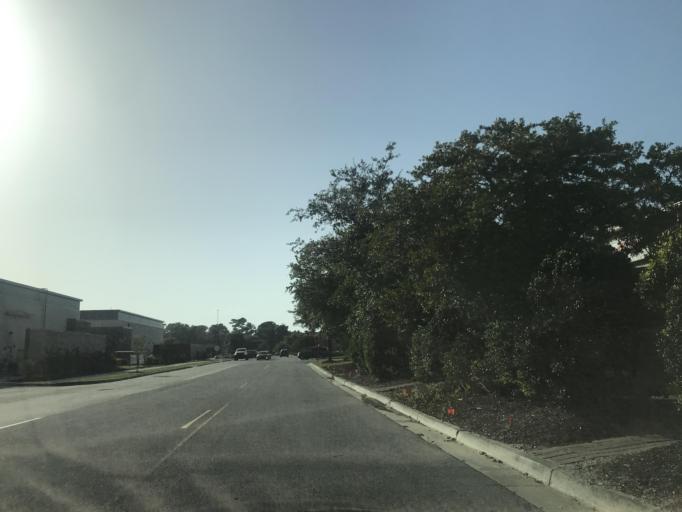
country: US
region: North Carolina
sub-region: New Hanover County
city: Wilmington
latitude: 34.2152
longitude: -77.9040
